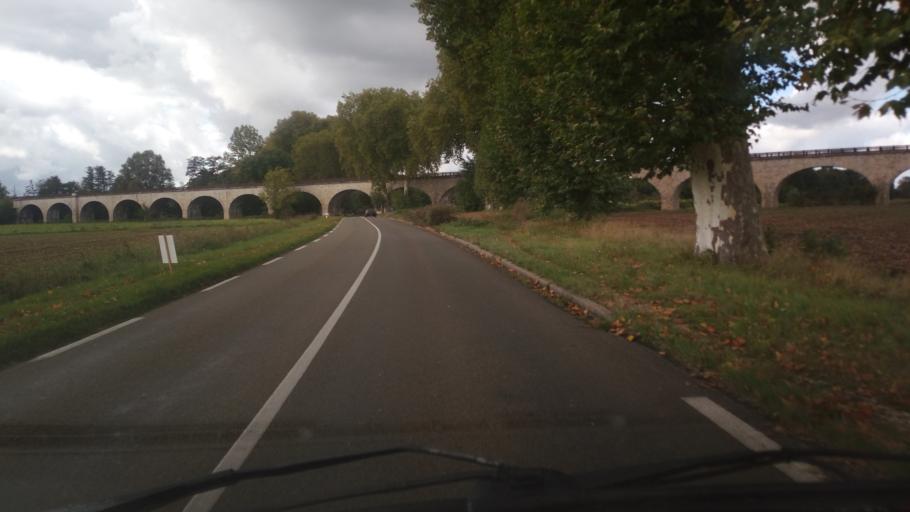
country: FR
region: Centre
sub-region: Departement du Loiret
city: Poilly-lez-Gien
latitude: 47.6814
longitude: 2.6126
